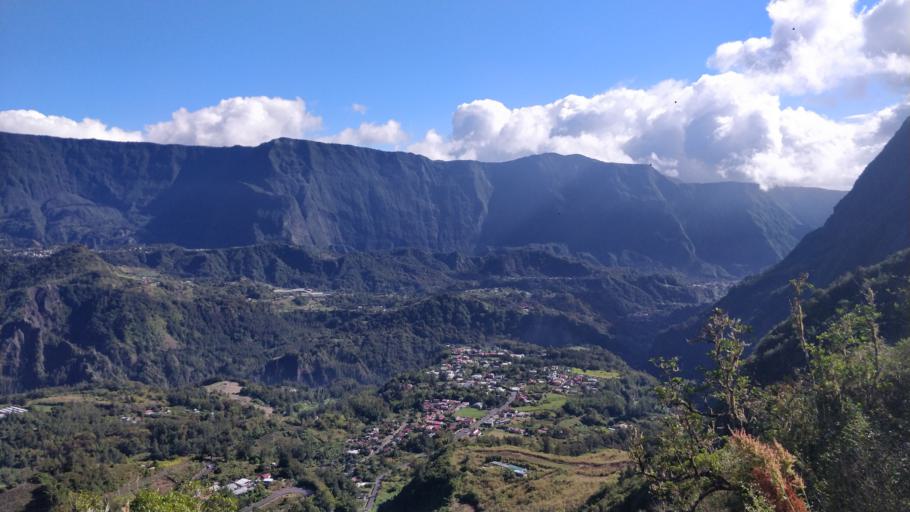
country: RE
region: Reunion
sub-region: Reunion
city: Salazie
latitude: -21.0620
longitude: 55.5301
